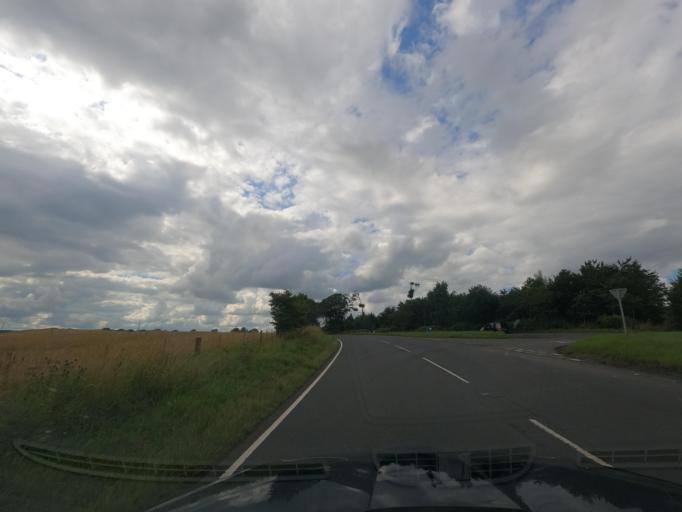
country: GB
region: Scotland
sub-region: The Scottish Borders
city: Duns
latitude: 55.7032
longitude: -2.4149
